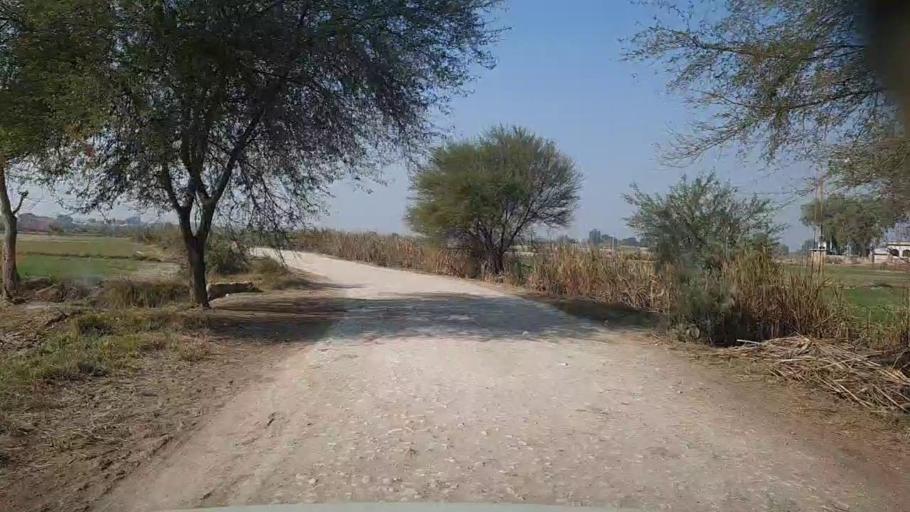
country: PK
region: Sindh
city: Khairpur
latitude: 27.9488
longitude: 69.7293
